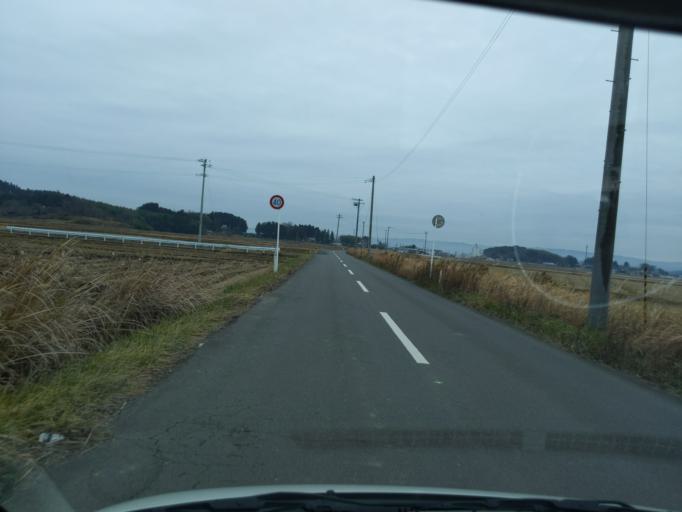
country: JP
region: Miyagi
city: Wakuya
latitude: 38.7217
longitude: 141.2170
